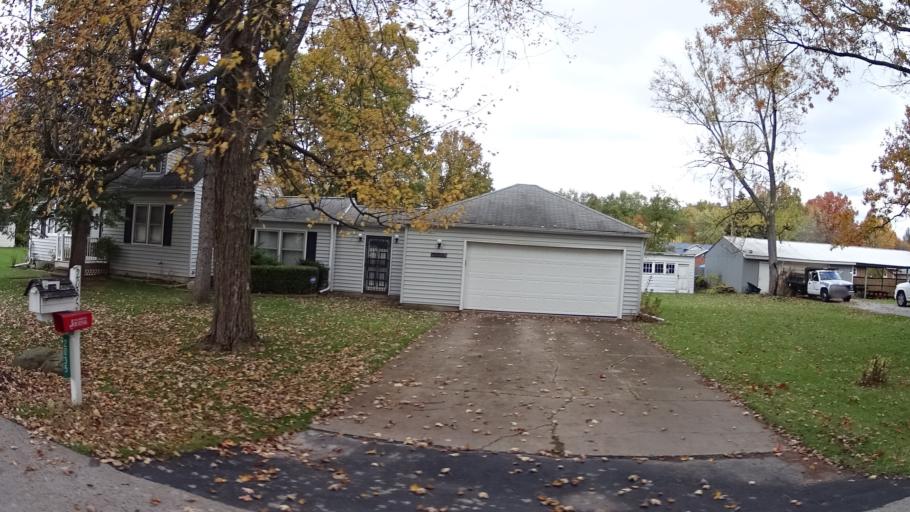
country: US
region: Ohio
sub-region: Lorain County
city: Sheffield
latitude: 41.4230
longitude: -82.1254
